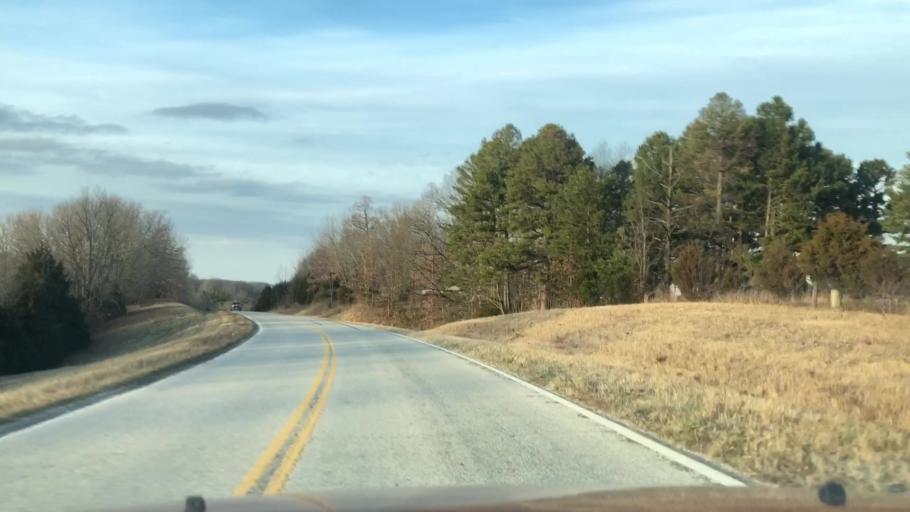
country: US
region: Missouri
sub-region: Webster County
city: Marshfield
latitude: 37.2358
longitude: -92.8790
